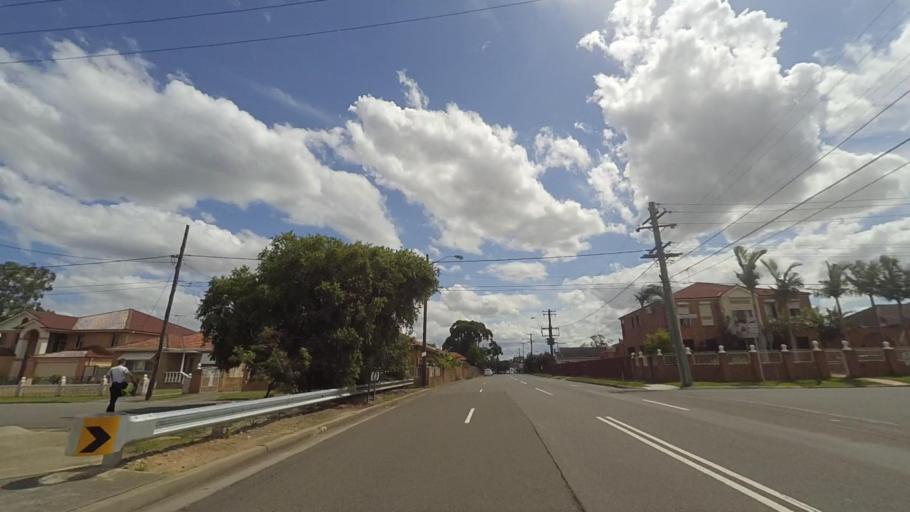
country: AU
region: New South Wales
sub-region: Fairfield
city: Fairfield East
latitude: -33.8629
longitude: 150.9565
